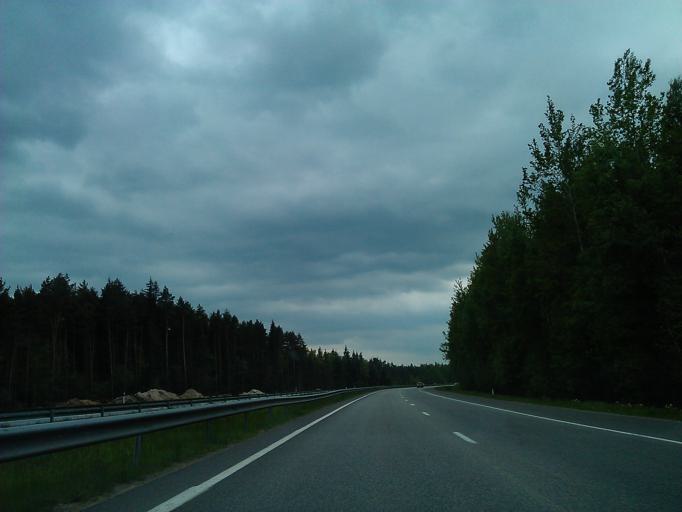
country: LV
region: Marupe
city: Marupe
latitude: 56.8490
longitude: 24.0613
